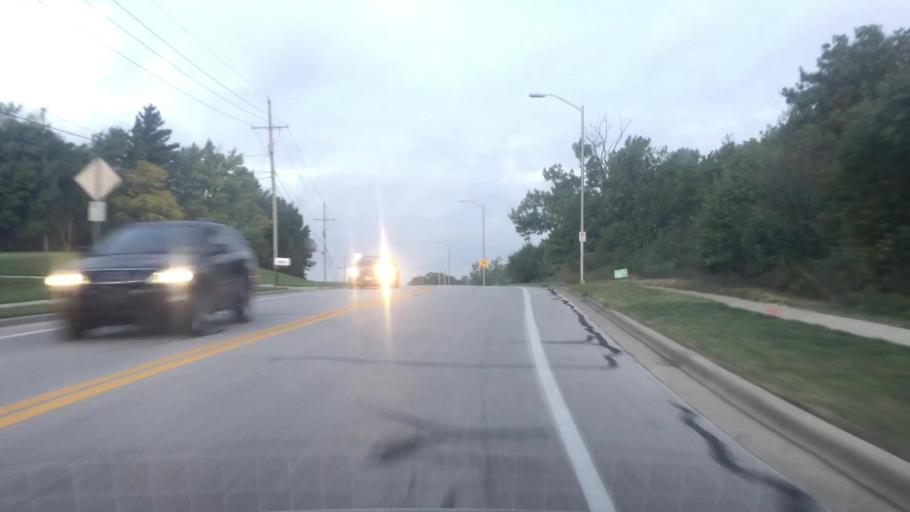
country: US
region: Kansas
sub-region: Johnson County
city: Shawnee
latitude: 39.0366
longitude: -94.7424
